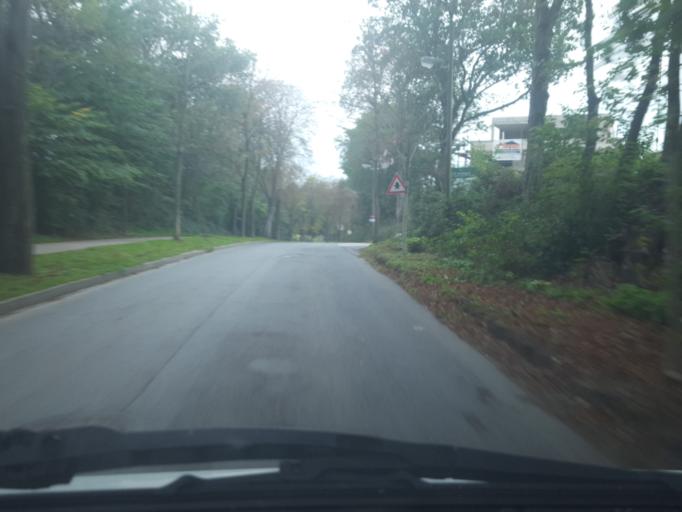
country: DE
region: North Rhine-Westphalia
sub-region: Regierungsbezirk Dusseldorf
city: Velbert
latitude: 51.3784
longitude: 7.0087
